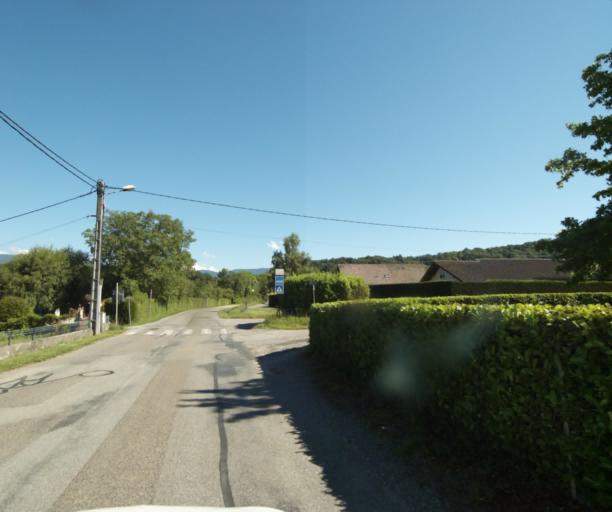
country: FR
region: Rhone-Alpes
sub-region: Departement de la Haute-Savoie
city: Sciez
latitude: 46.3264
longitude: 6.3805
